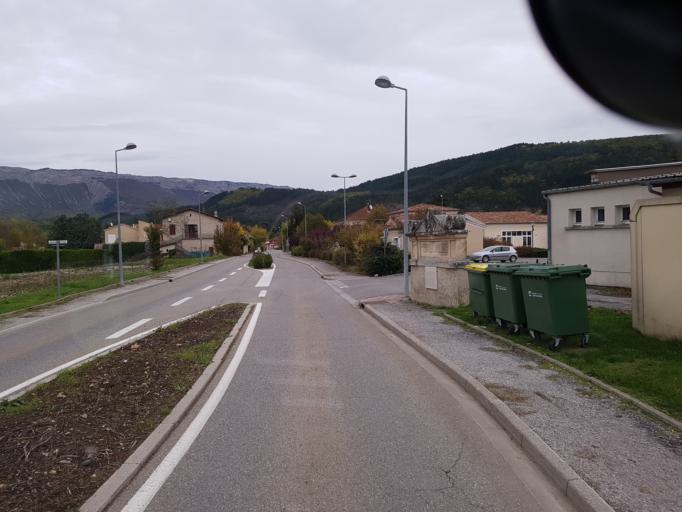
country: FR
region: Provence-Alpes-Cote d'Azur
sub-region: Departement des Hautes-Alpes
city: Laragne-Monteglin
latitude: 44.3424
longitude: 5.7662
